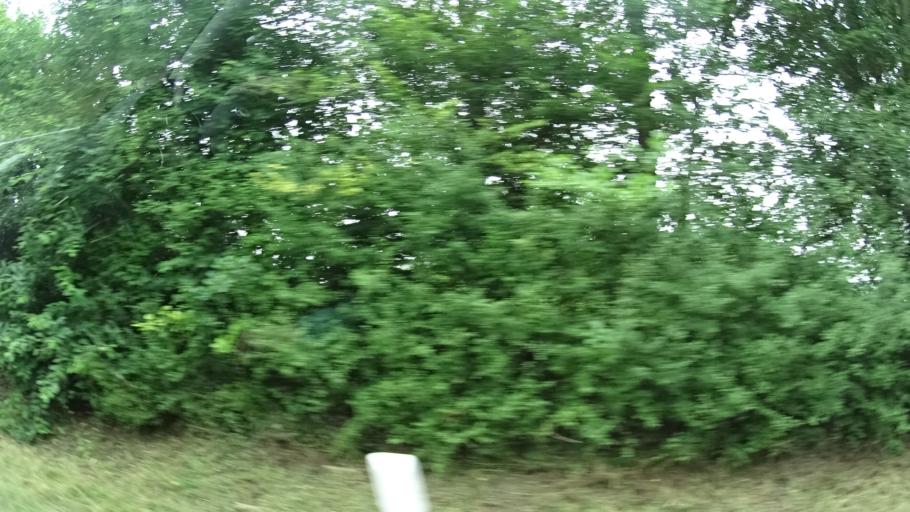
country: DE
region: Saarland
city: Orscholz
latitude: 49.4466
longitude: 6.5475
